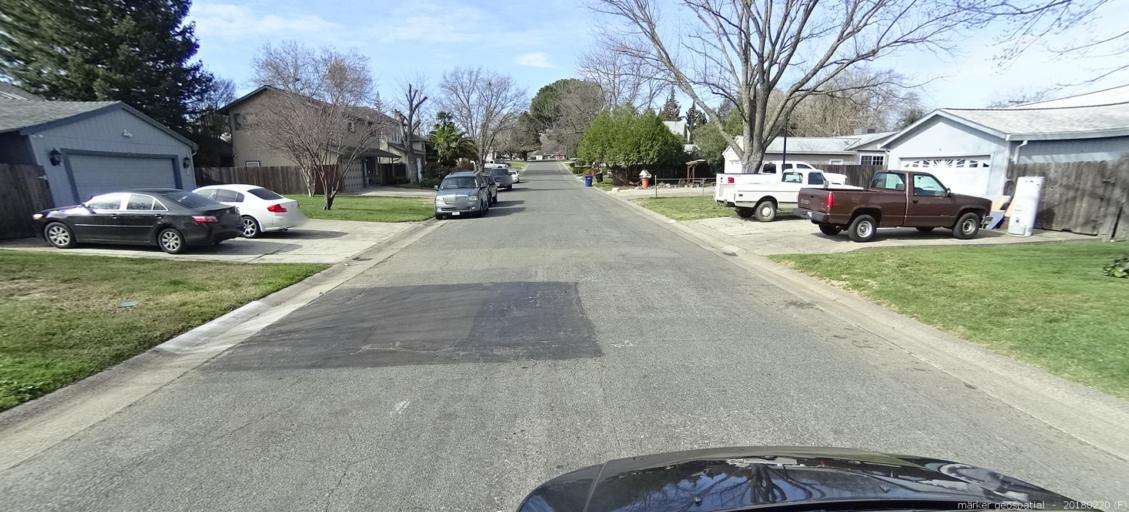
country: US
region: California
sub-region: Sacramento County
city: Orangevale
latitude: 38.6754
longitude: -121.2280
